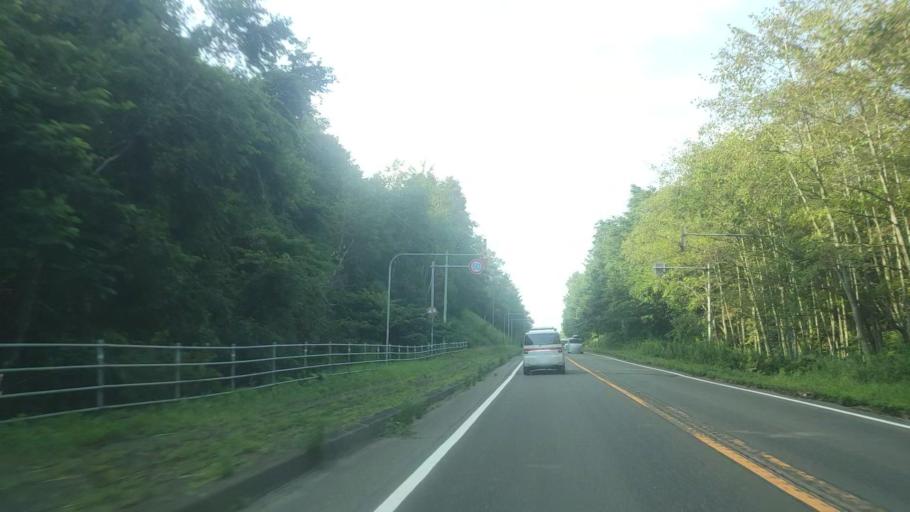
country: JP
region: Hokkaido
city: Chitose
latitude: 42.8635
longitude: 141.8225
